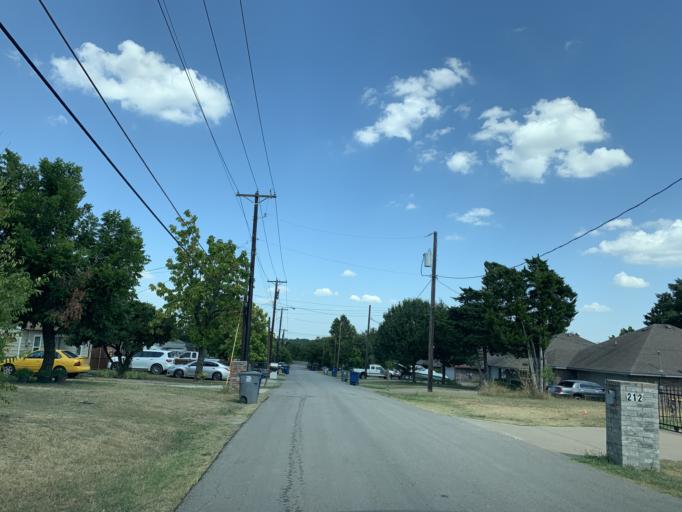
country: US
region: Texas
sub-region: Dallas County
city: DeSoto
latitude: 32.6636
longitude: -96.8210
